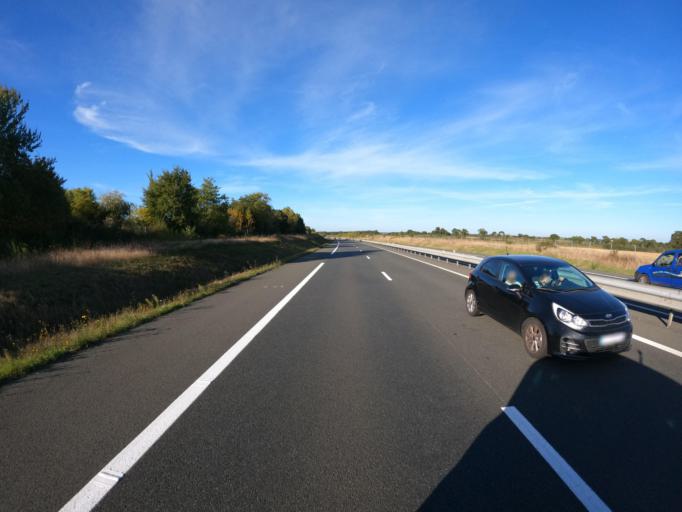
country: FR
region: Pays de la Loire
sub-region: Departement de Maine-et-Loire
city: Saint-Lambert-du-Lattay
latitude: 47.2606
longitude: -0.6161
